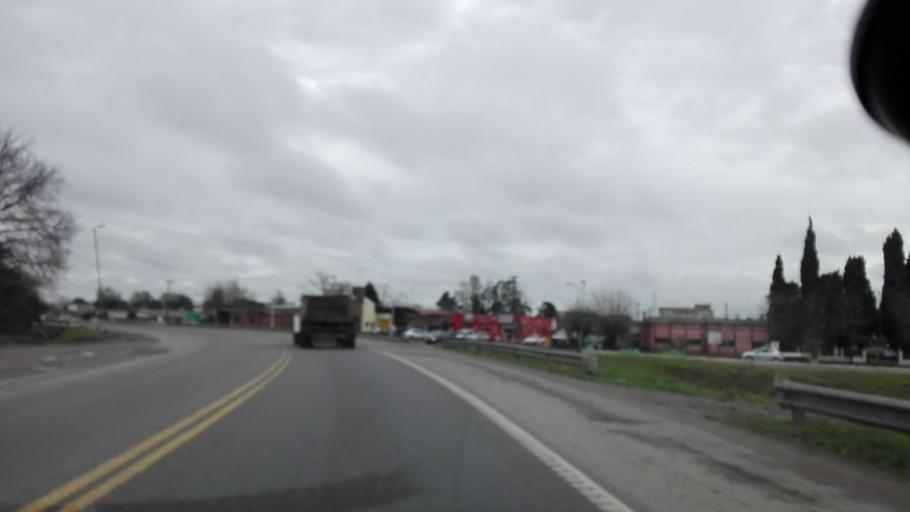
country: AR
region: Buenos Aires
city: San Miguel del Monte
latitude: -35.4456
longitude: -58.8164
